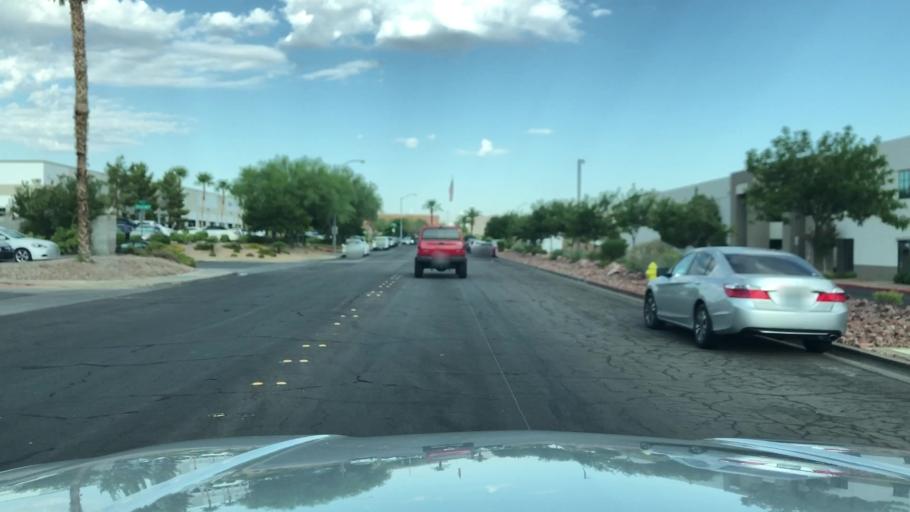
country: US
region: Nevada
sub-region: Clark County
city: Henderson
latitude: 36.0381
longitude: -115.0334
